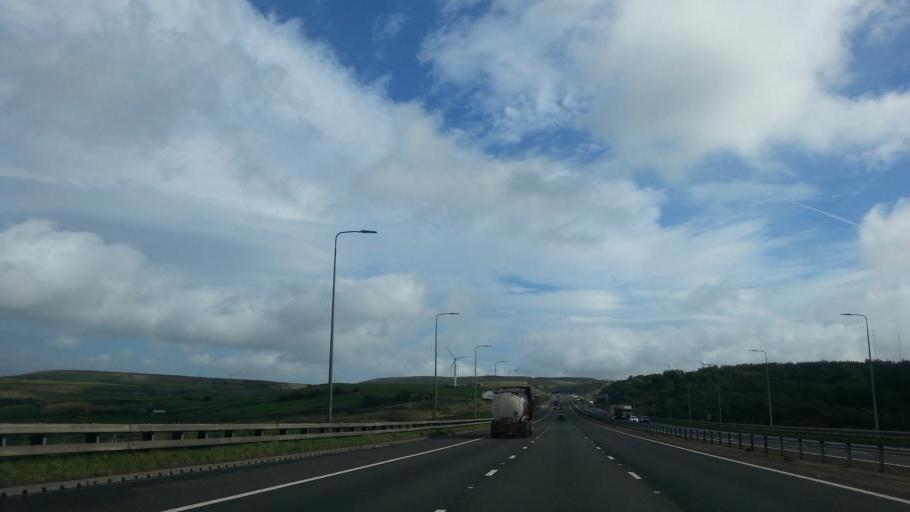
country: GB
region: England
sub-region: Calderdale
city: Ripponden
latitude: 53.6472
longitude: -1.9237
